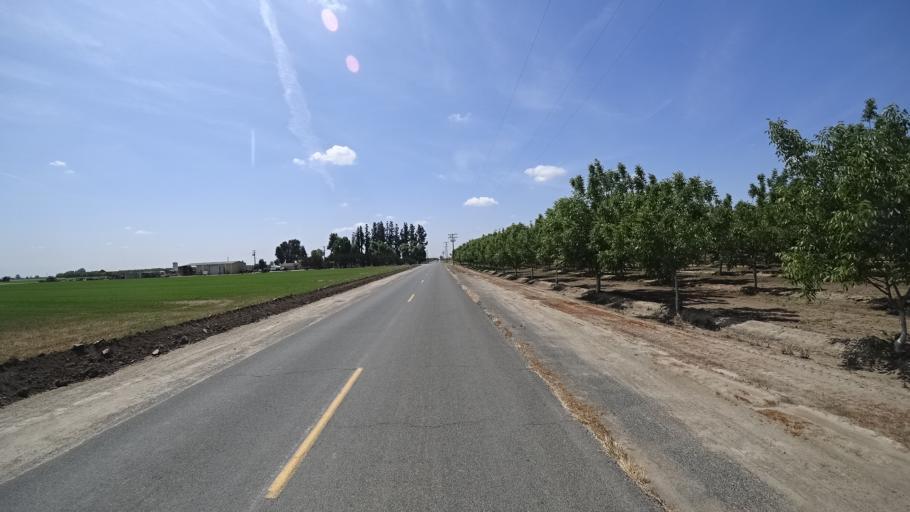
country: US
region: California
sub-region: Tulare County
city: Goshen
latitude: 36.3260
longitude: -119.4842
